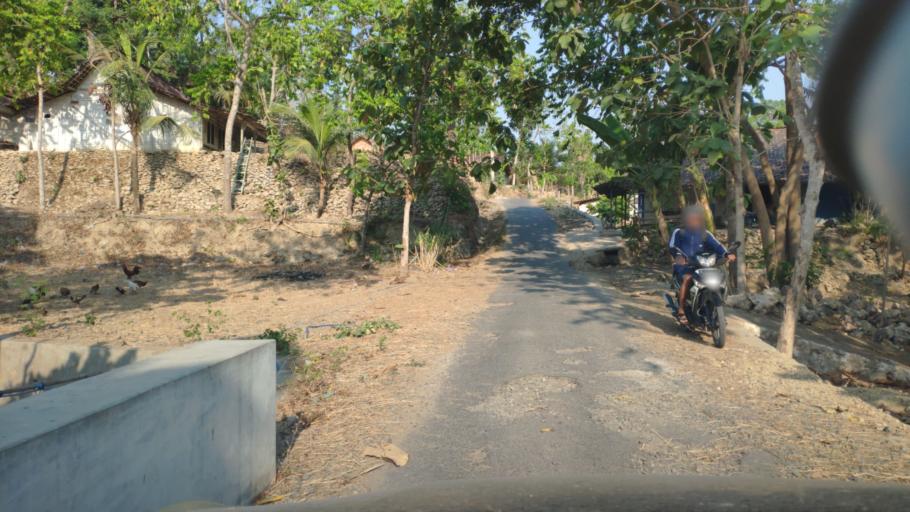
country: ID
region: Central Java
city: Nglengkir
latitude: -6.9199
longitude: 111.5116
